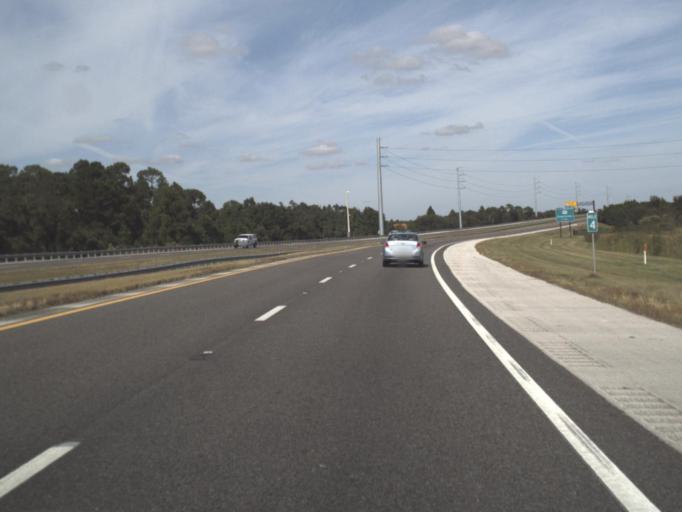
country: US
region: Florida
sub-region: Polk County
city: Citrus Ridge
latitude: 28.3248
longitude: -81.6138
